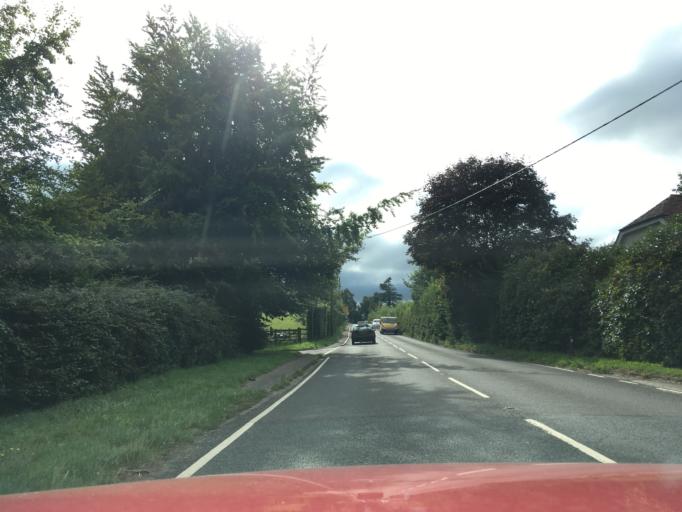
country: GB
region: England
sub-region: West Sussex
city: Milland
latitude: 51.0084
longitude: -0.8453
